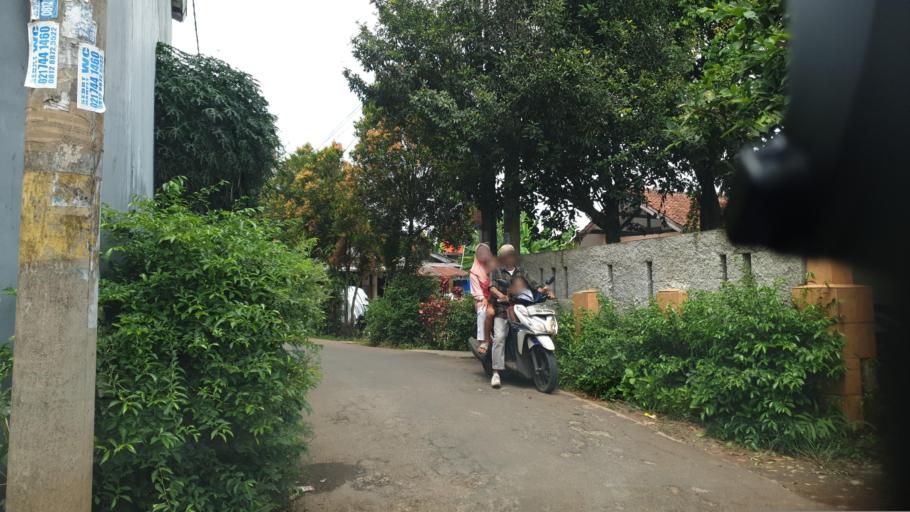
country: ID
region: West Java
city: Sawangan
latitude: -6.3777
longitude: 106.7641
